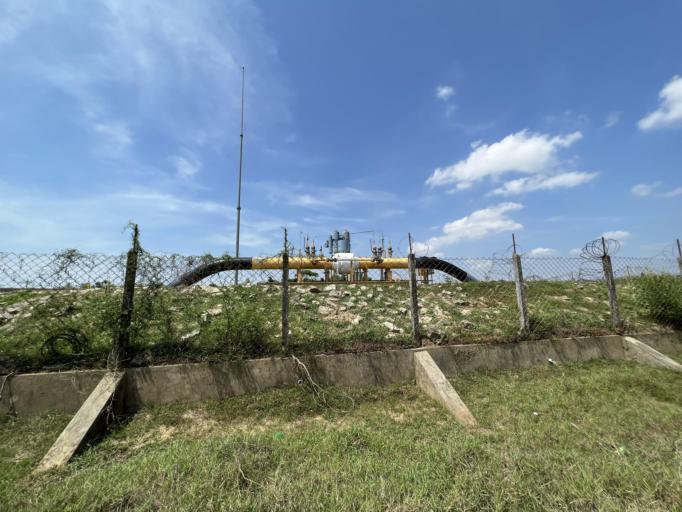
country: MM
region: Ayeyarwady
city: Pyapon
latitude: 15.9008
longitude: 95.6113
